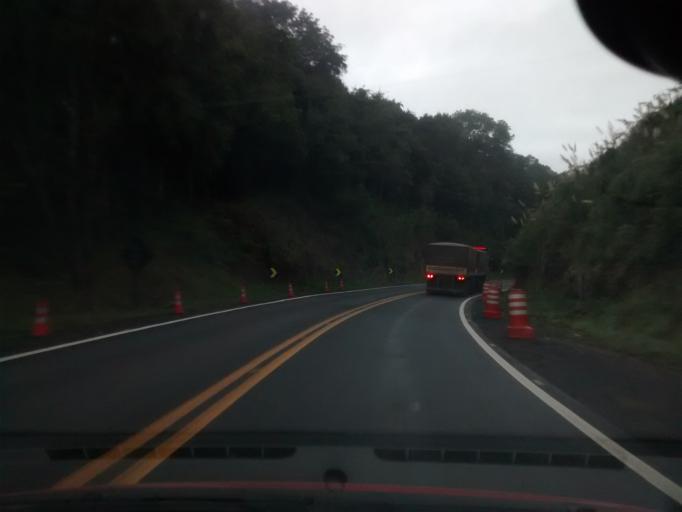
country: BR
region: Rio Grande do Sul
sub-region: Vacaria
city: Estrela
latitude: -28.1975
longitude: -50.7211
